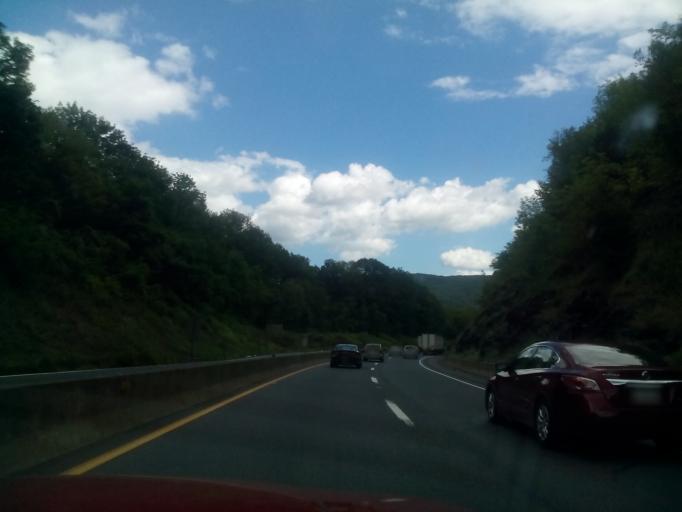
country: US
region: Pennsylvania
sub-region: Monroe County
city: East Stroudsburg
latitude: 40.9979
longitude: -75.1470
